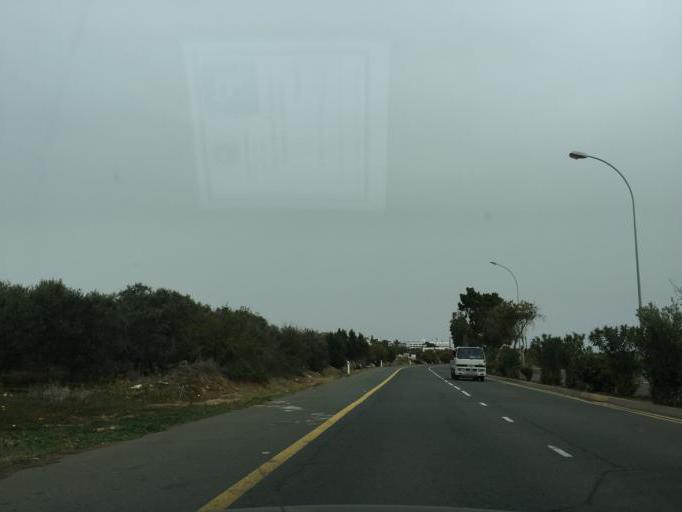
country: CY
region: Ammochostos
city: Ayia Napa
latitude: 34.9899
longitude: 34.0070
